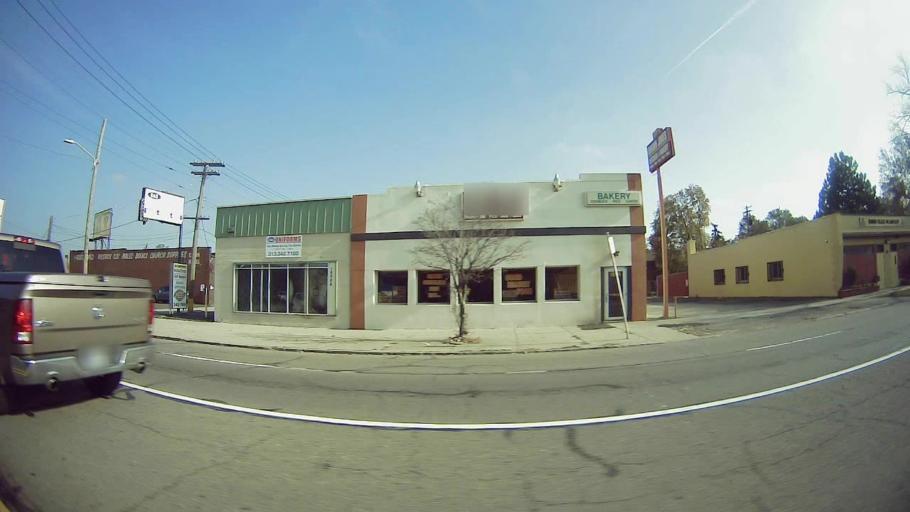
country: US
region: Michigan
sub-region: Oakland County
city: Oak Park
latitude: 42.4305
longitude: -83.1806
